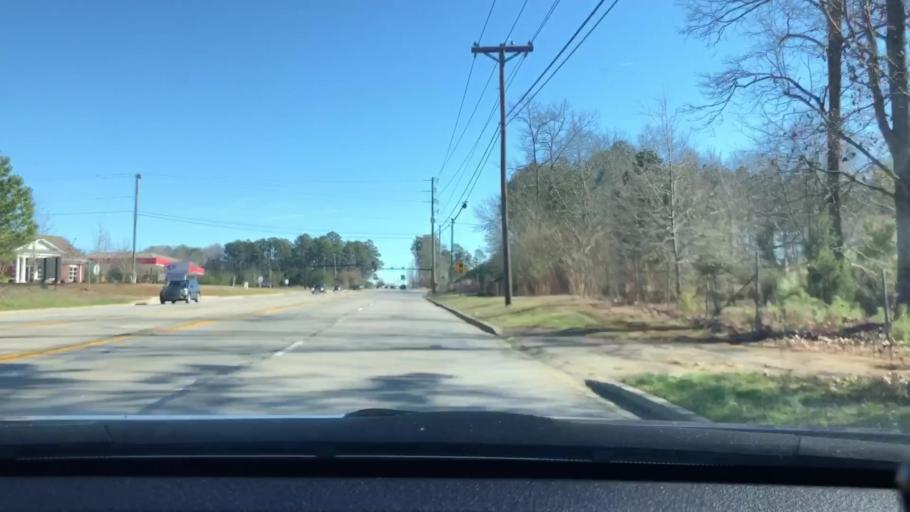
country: US
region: South Carolina
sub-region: Lexington County
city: Oak Grove
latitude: 34.0136
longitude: -81.1625
